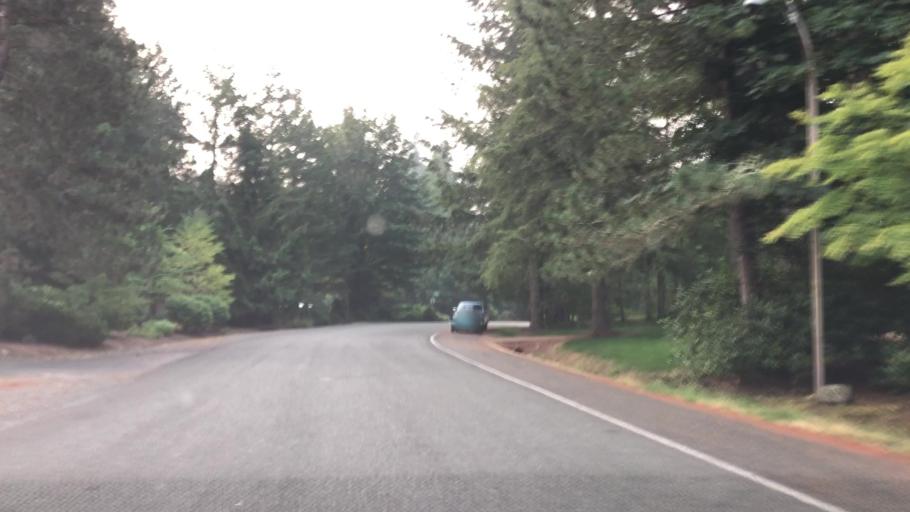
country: US
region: Washington
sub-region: King County
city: Cottage Lake
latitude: 47.7245
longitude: -122.1005
